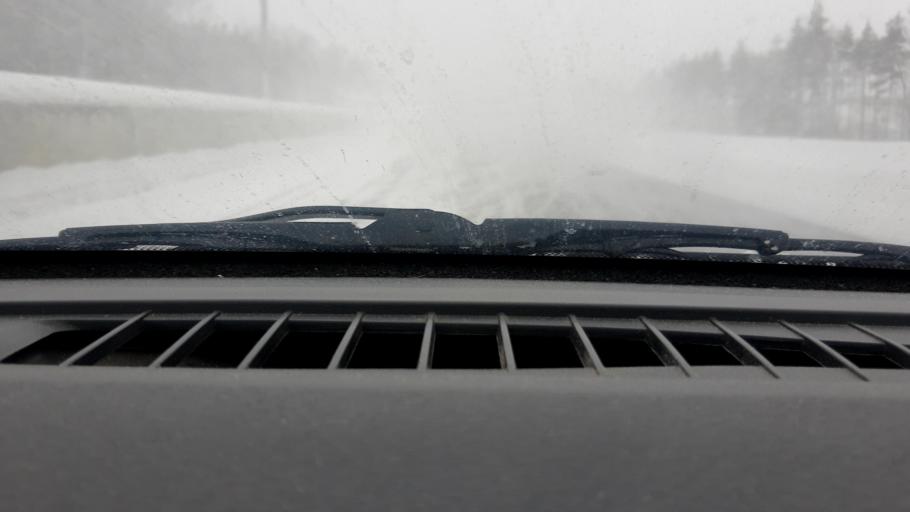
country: RU
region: Moskovskaya
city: Krasnoarmeysk
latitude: 56.0658
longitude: 38.0957
